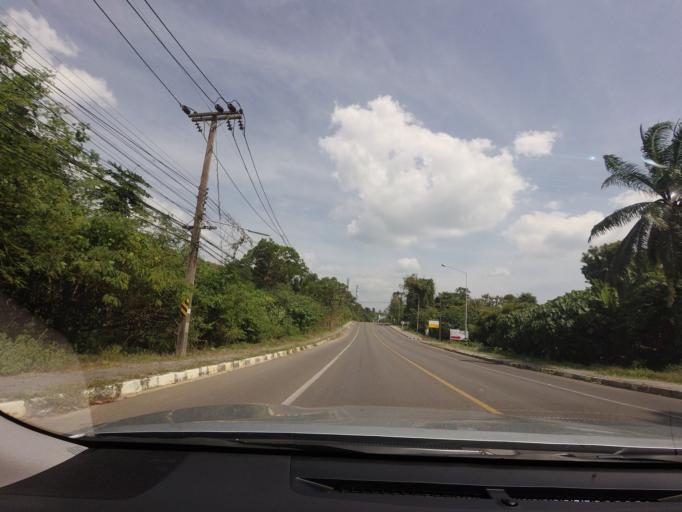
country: TH
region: Phangnga
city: Ban Ao Nang
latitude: 8.0552
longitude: 98.7536
